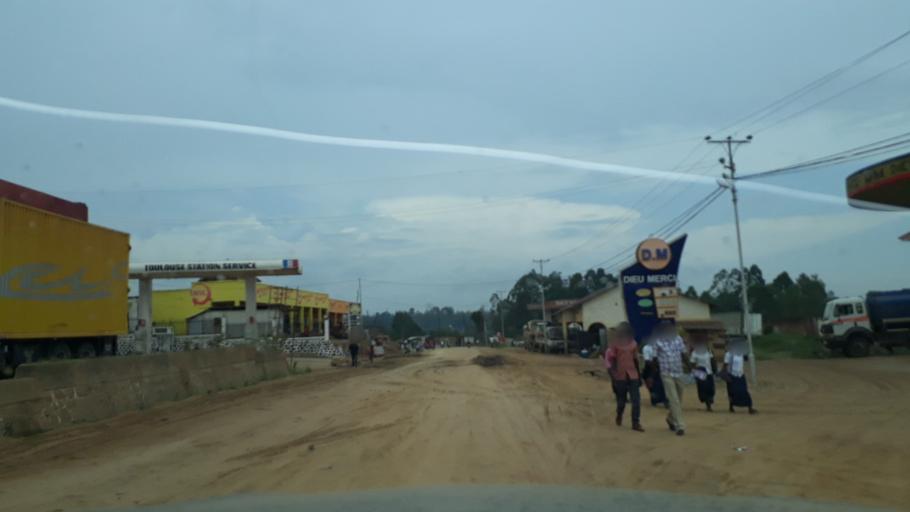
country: CD
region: Eastern Province
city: Bunia
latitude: 1.5724
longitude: 30.2473
